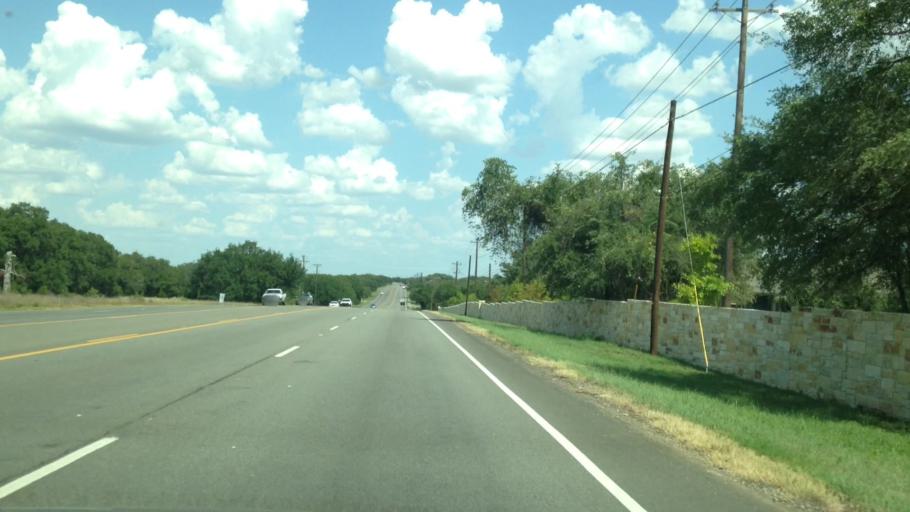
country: US
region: Texas
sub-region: Williamson County
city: Georgetown
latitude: 30.6321
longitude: -97.7610
